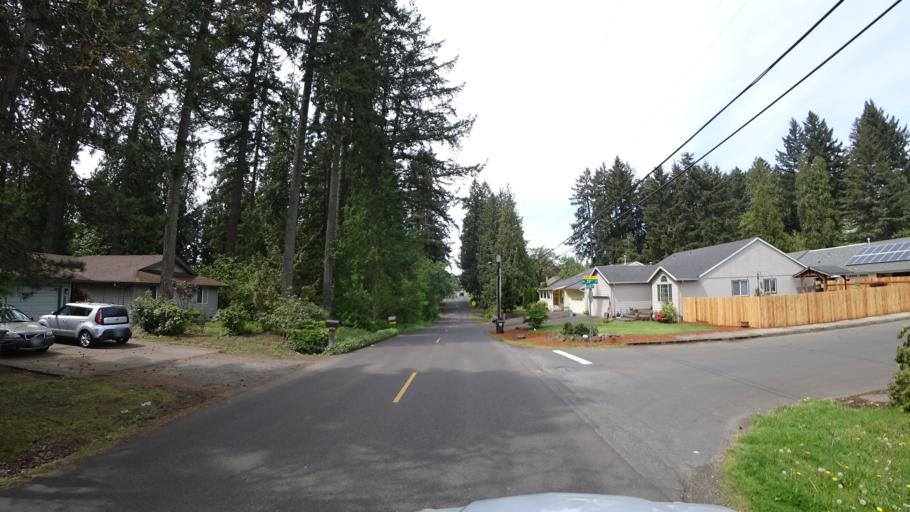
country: US
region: Oregon
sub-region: Washington County
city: Hillsboro
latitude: 45.5122
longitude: -122.9424
